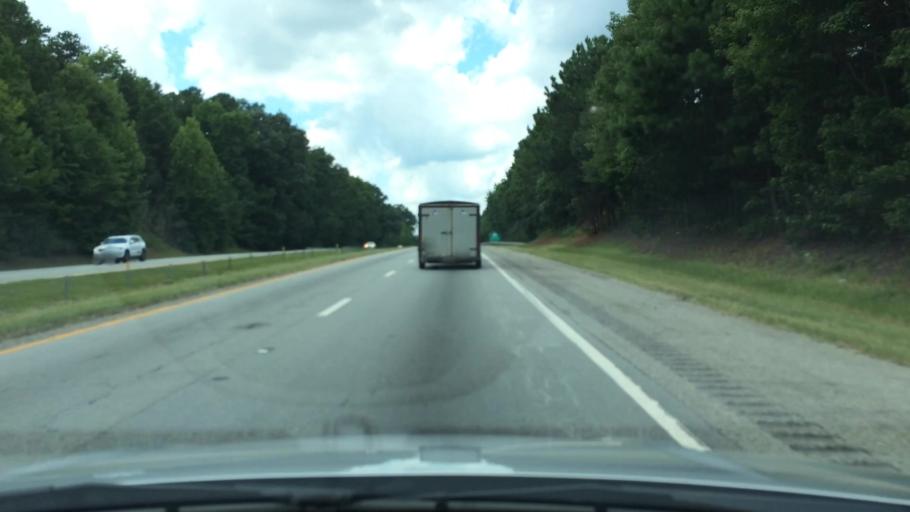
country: US
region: South Carolina
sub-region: Lexington County
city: Chapin
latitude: 34.2133
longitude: -81.3919
